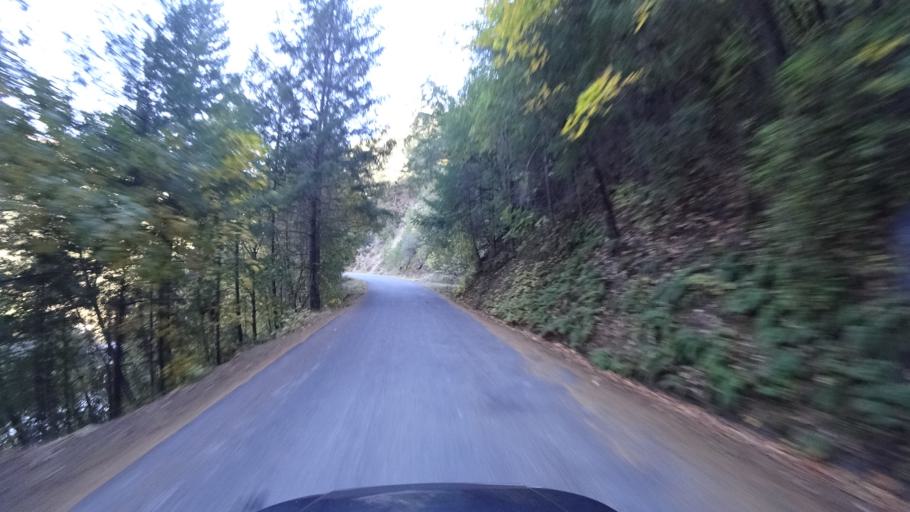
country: US
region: California
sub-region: Humboldt County
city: Willow Creek
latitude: 41.2510
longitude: -123.3149
